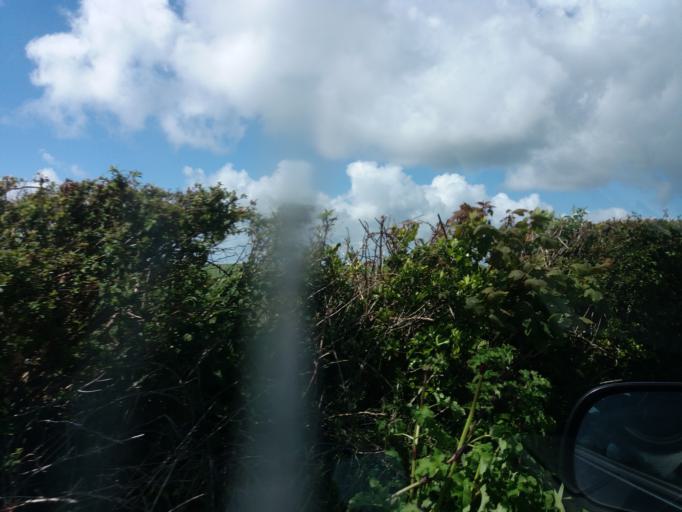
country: IE
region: Munster
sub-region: Waterford
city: Dunmore East
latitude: 52.1595
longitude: -6.8945
